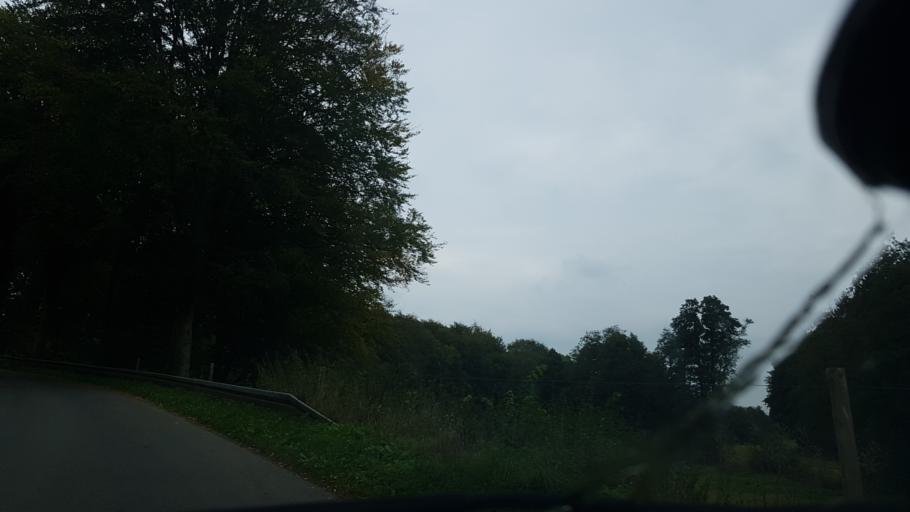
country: DK
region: South Denmark
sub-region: Kolding Kommune
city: Kolding
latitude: 55.5554
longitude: 9.4028
